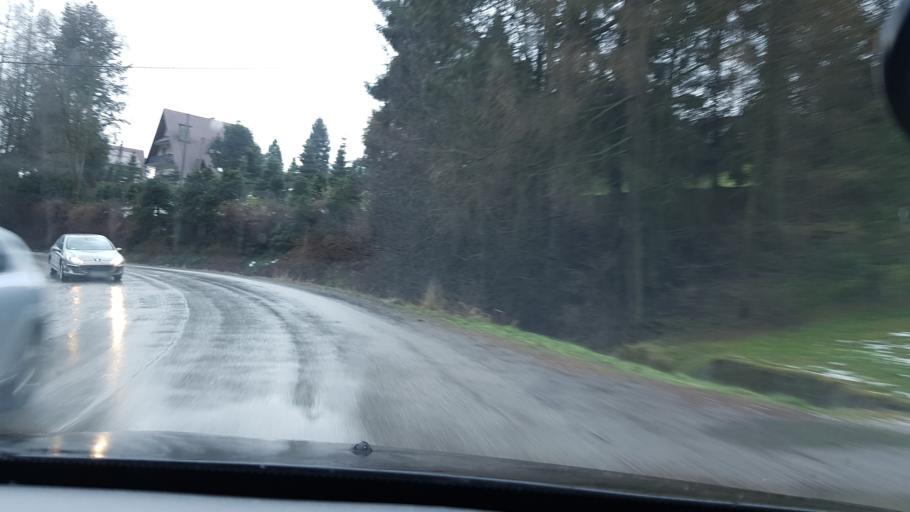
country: PL
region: Lesser Poland Voivodeship
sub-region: Powiat suski
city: Jordanow
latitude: 49.6378
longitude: 19.8278
